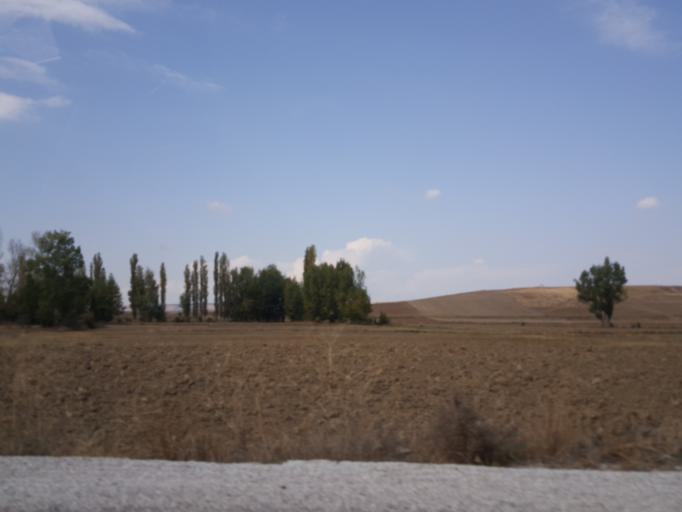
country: TR
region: Corum
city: Alaca
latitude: 40.1399
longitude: 34.8156
